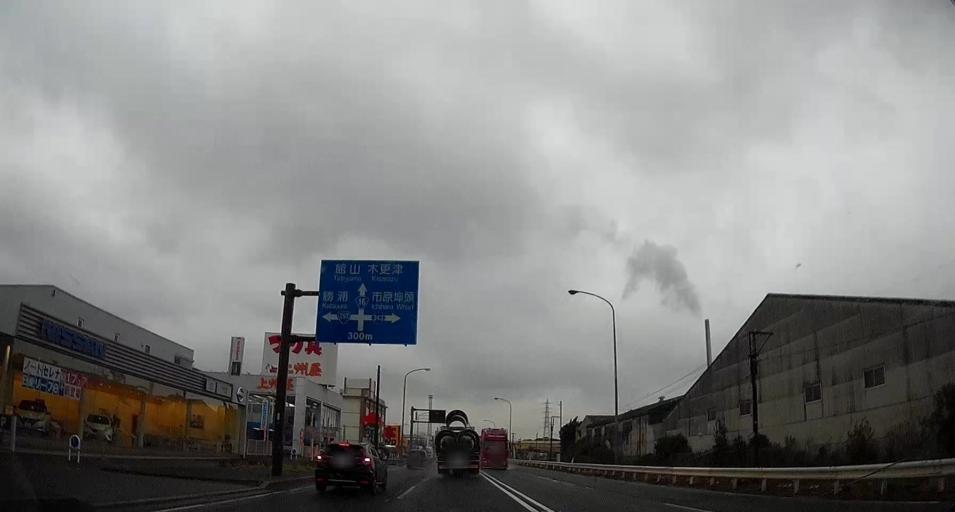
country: JP
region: Chiba
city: Ichihara
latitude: 35.5385
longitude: 140.1132
